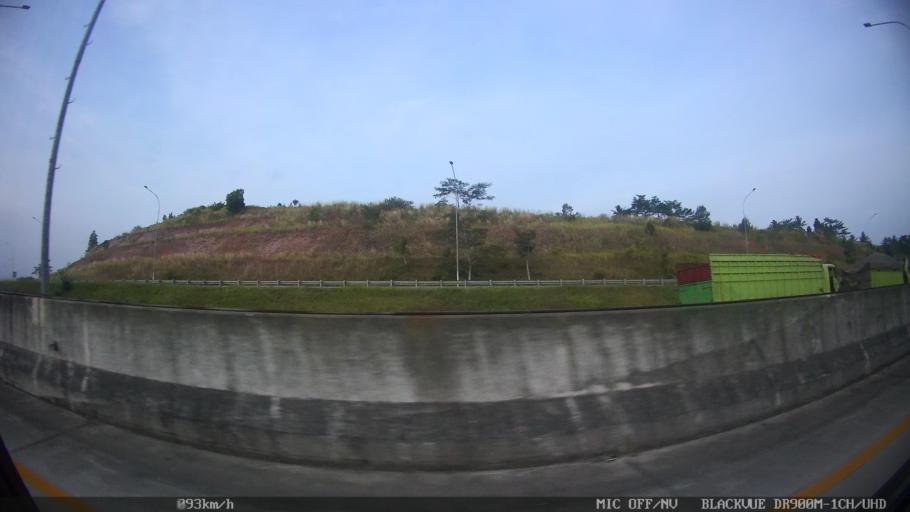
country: ID
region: Lampung
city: Penengahan
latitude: -5.8094
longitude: 105.7340
